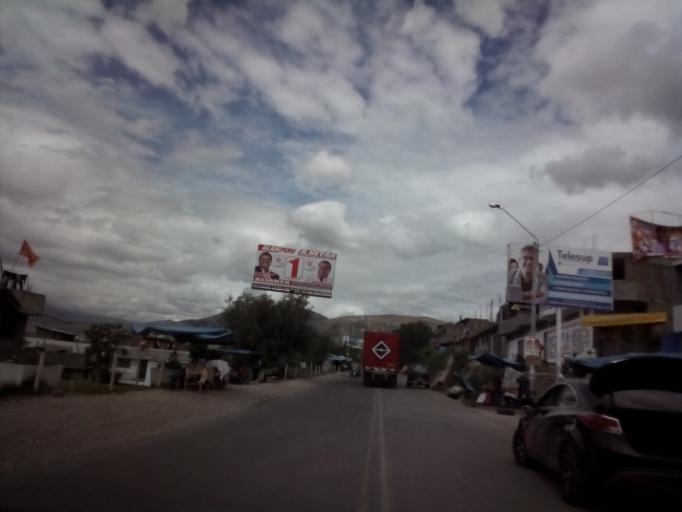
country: PE
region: Ayacucho
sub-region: Provincia de Huamanga
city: Ayacucho
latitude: -13.1482
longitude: -74.2353
